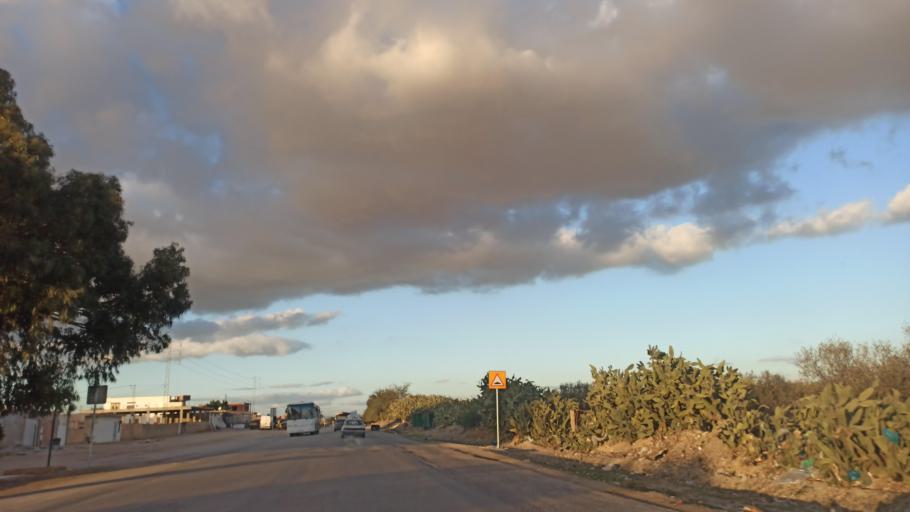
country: TN
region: Susah
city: Sidi Bou Ali
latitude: 36.0079
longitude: 10.3173
